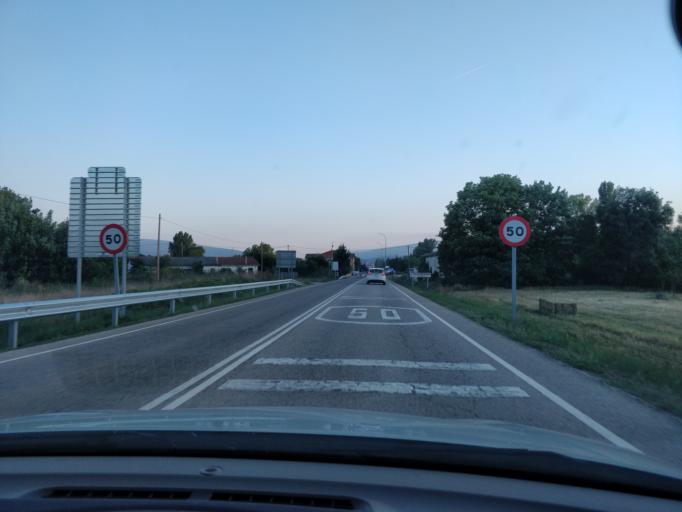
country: ES
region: Castille and Leon
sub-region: Provincia de Burgos
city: Medina de Pomar
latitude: 42.9532
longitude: -3.5591
